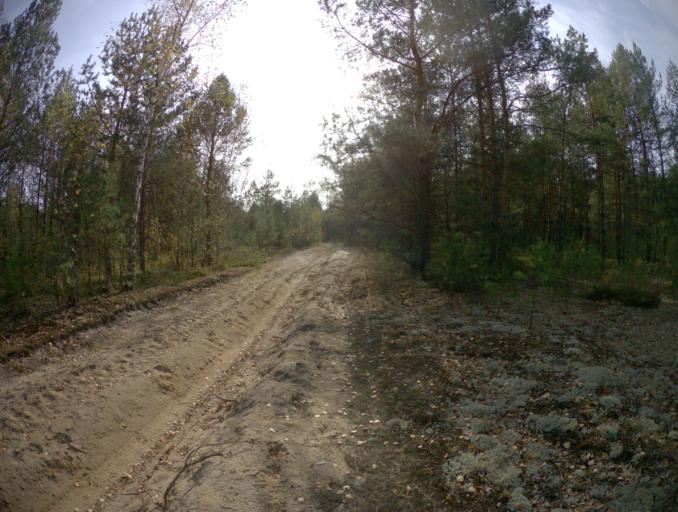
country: RU
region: Vladimir
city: Sobinka
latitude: 55.9381
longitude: 40.0459
